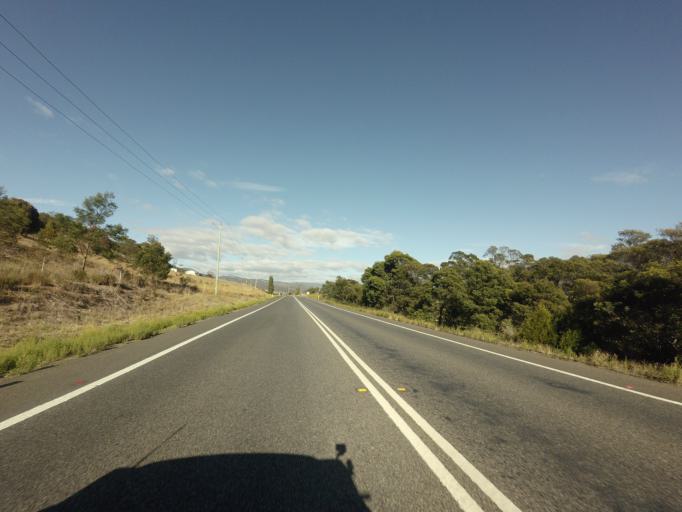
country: AU
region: Tasmania
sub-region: Glenorchy
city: Granton
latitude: -42.7589
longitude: 147.1489
